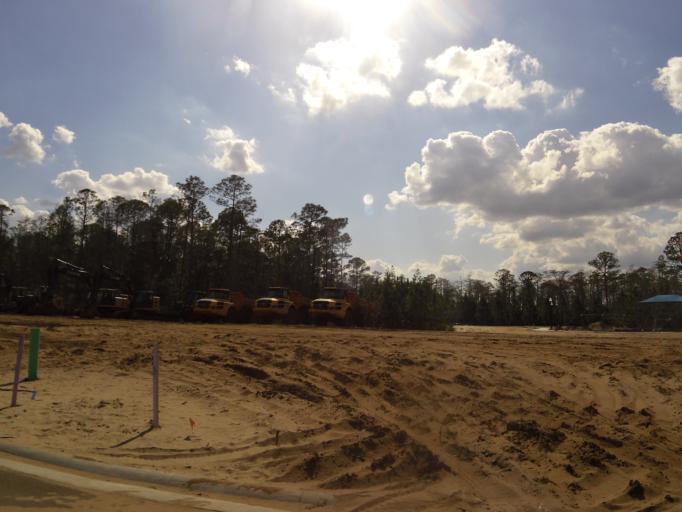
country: US
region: Florida
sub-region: Saint Johns County
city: Palm Valley
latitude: 30.1874
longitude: -81.5000
